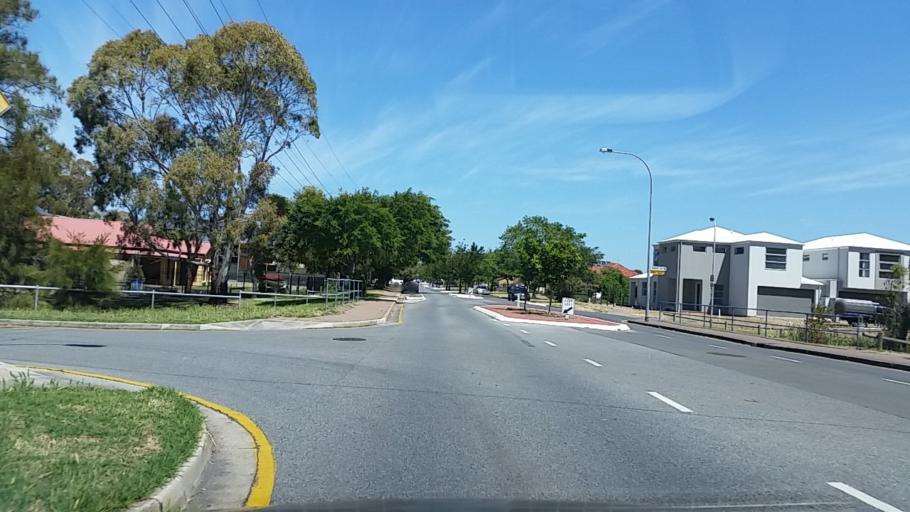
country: AU
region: South Australia
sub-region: Charles Sturt
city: Grange
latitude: -34.9047
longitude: 138.5004
